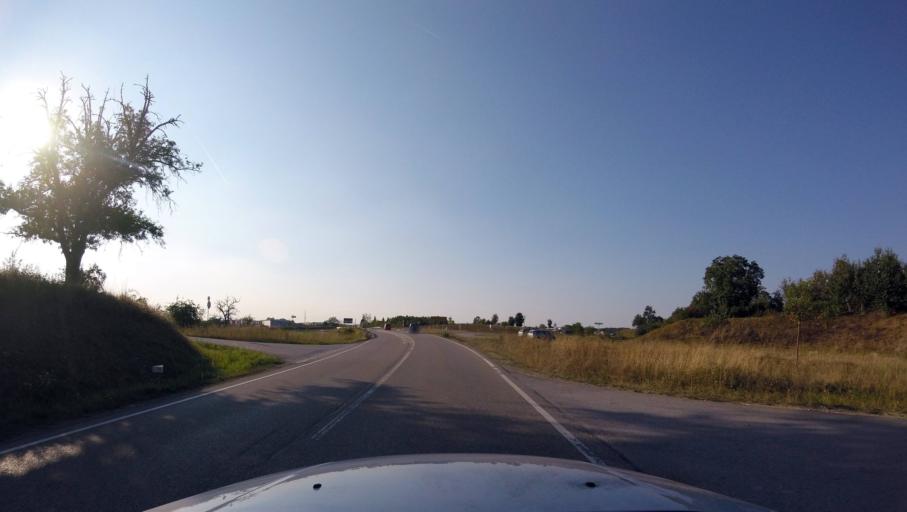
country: DE
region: Baden-Wuerttemberg
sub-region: Regierungsbezirk Stuttgart
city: Leutenbach
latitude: 48.8997
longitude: 9.4214
